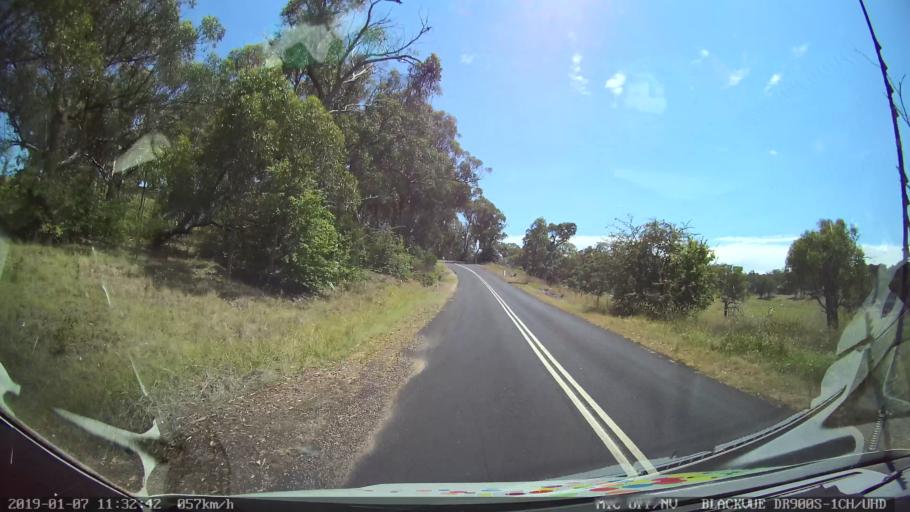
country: AU
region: New South Wales
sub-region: Armidale Dumaresq
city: Armidale
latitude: -30.4068
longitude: 151.5600
